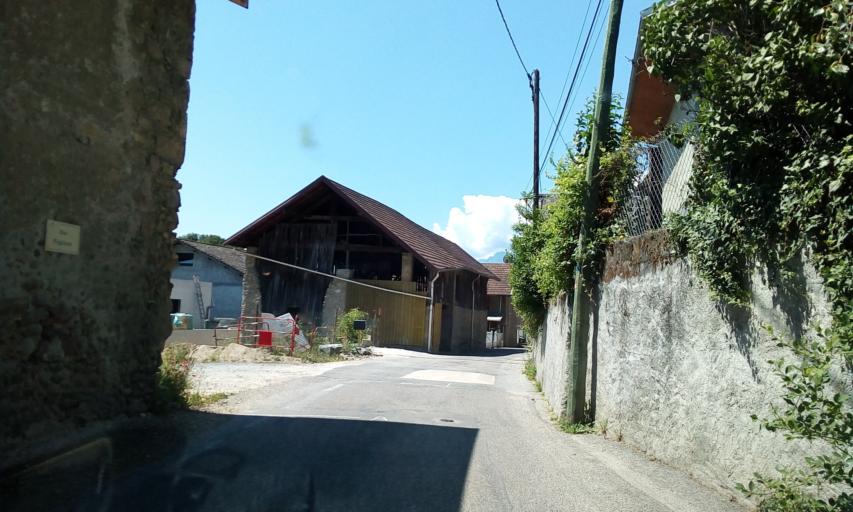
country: FR
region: Rhone-Alpes
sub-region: Departement de la Savoie
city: Montmelian
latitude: 45.4782
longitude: 6.0579
